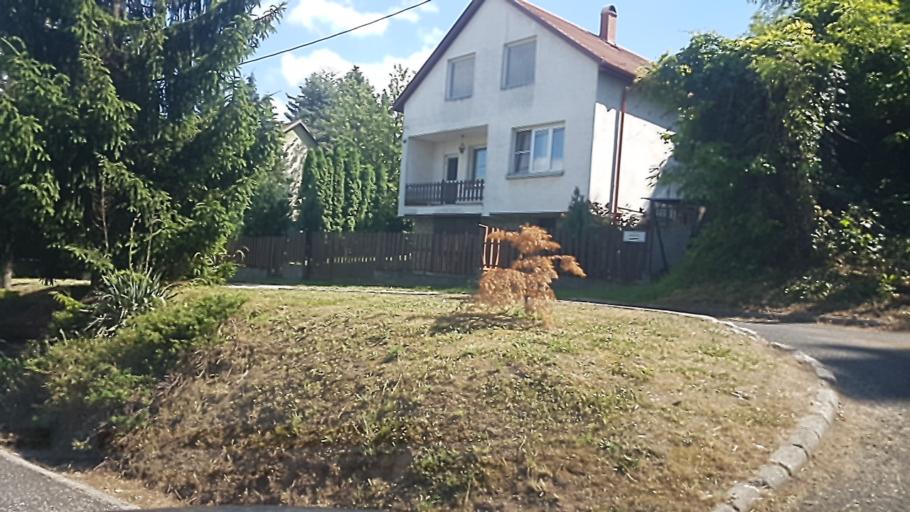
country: HU
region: Pest
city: Pilisszentivan
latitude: 47.6100
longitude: 18.8888
